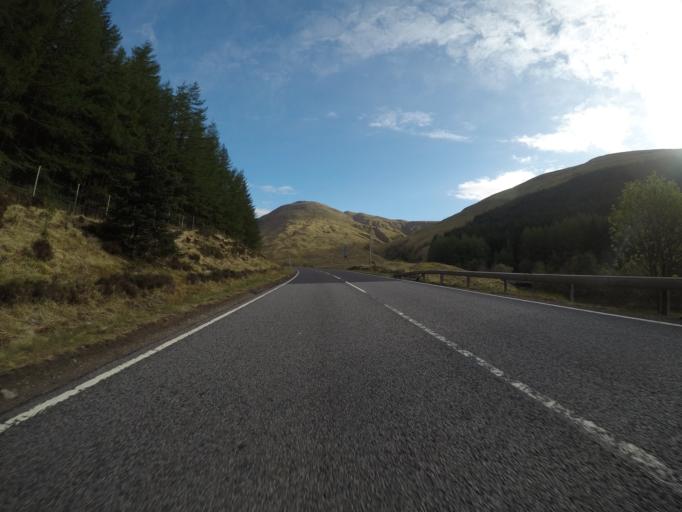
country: GB
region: Scotland
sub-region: Argyll and Bute
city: Garelochhead
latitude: 56.4471
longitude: -4.7099
